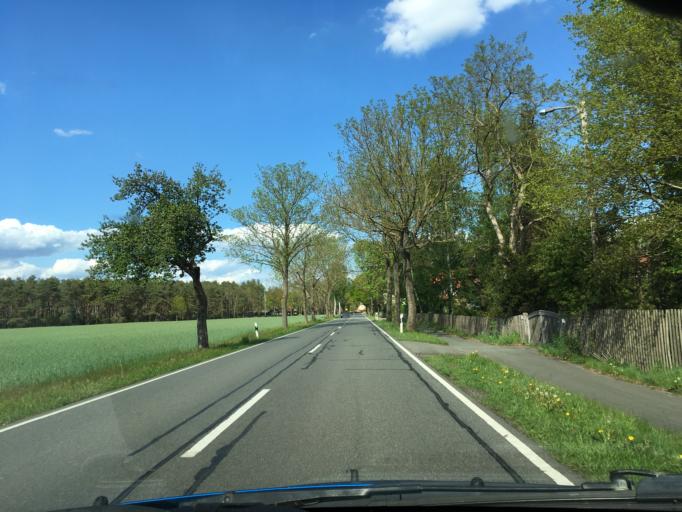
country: DE
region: Lower Saxony
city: Trebel
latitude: 52.9892
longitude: 11.3043
